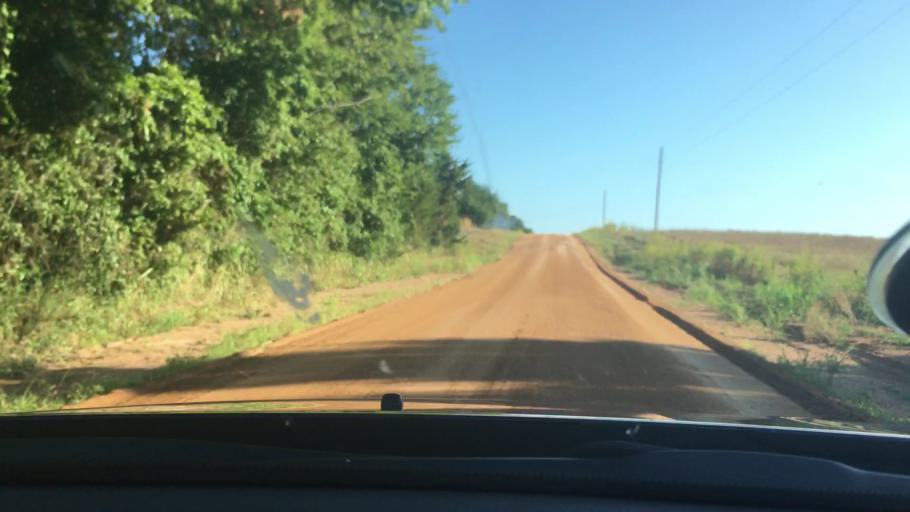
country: US
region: Oklahoma
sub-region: Murray County
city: Sulphur
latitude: 34.4124
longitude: -96.7936
